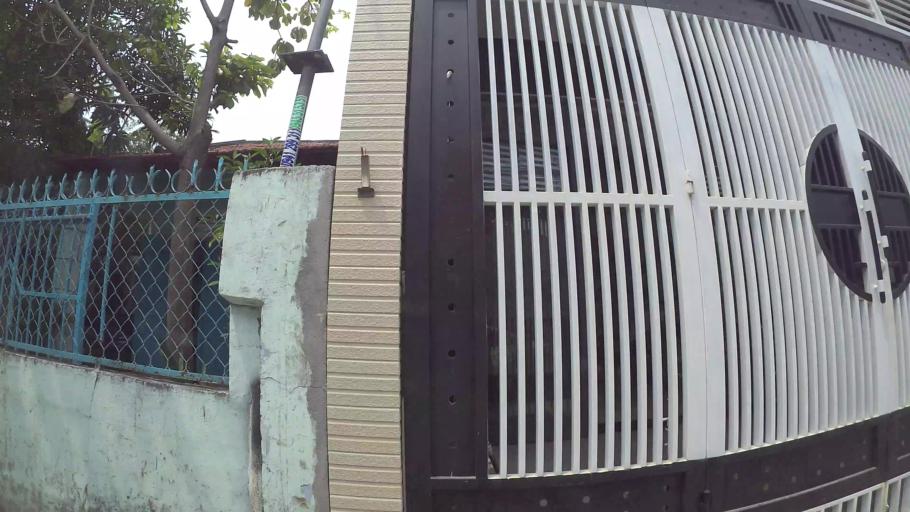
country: VN
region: Da Nang
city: Son Tra
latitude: 16.0986
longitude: 108.2496
